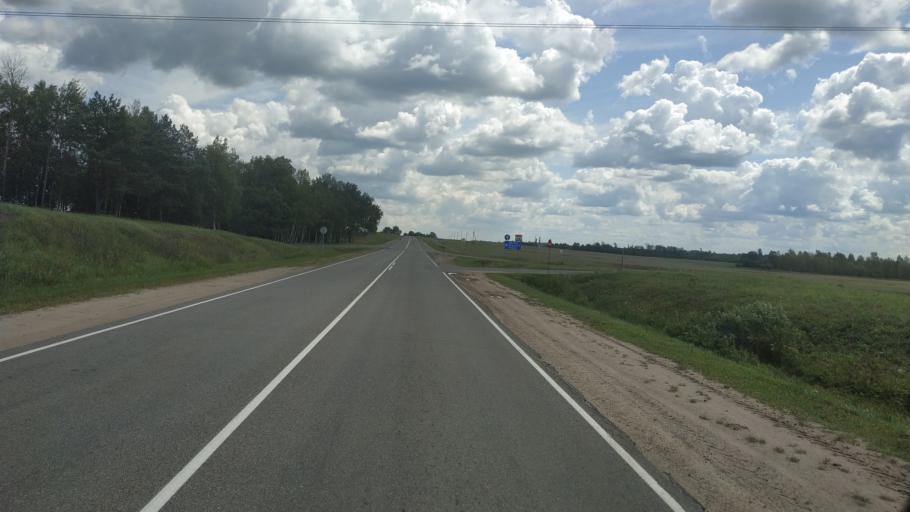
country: BY
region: Mogilev
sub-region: Mahilyowski Rayon
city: Veyno
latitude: 53.8120
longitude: 30.4589
